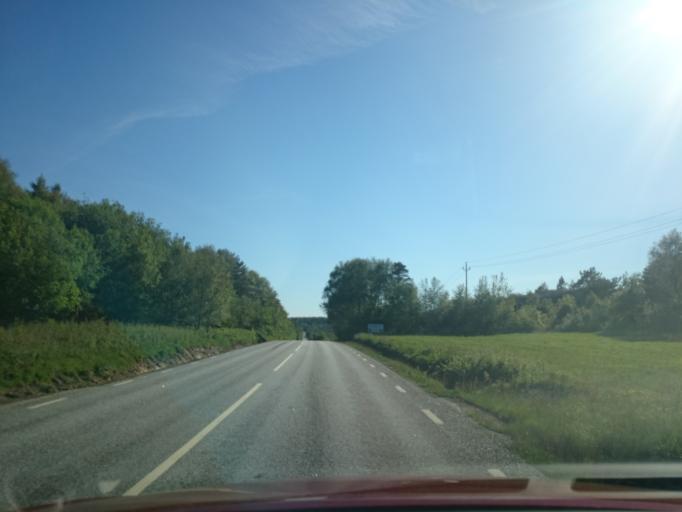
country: SE
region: Vaestra Goetaland
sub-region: Lysekils Kommun
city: Lysekil
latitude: 58.2859
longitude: 11.5446
